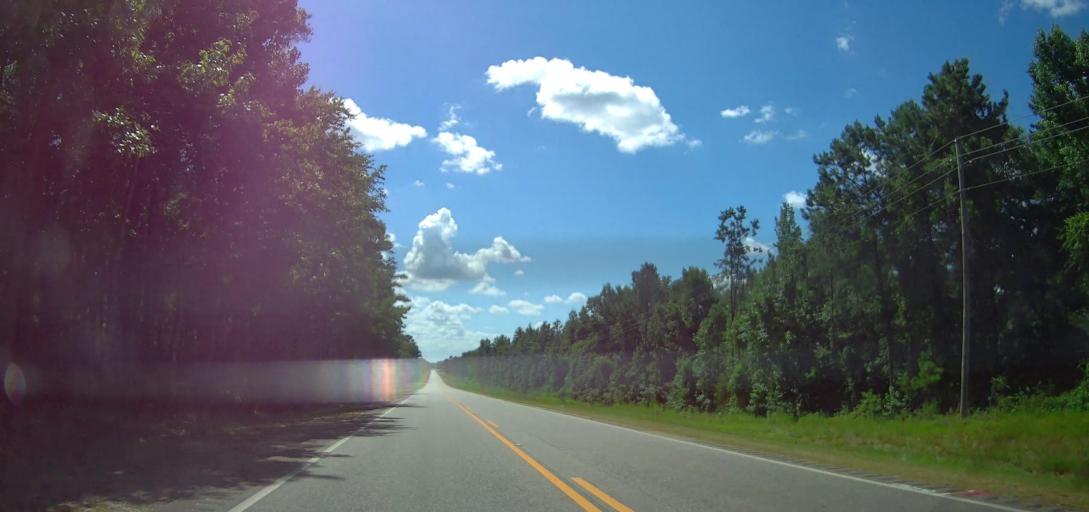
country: US
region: Alabama
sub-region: Elmore County
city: Tallassee
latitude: 32.3992
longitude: -85.9337
